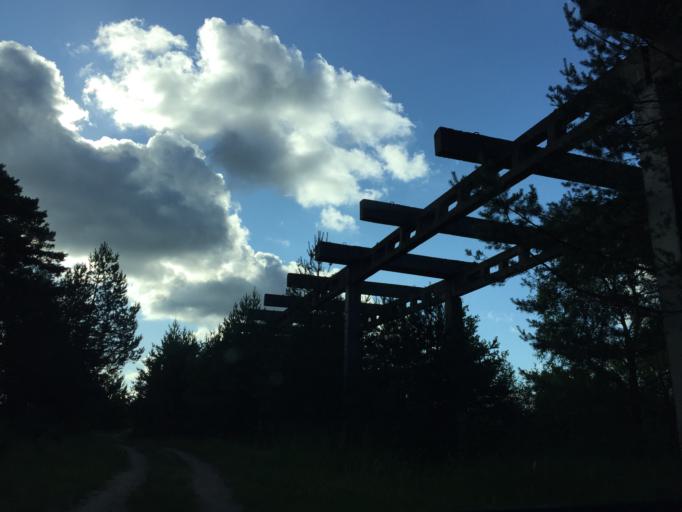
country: LV
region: Ventspils
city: Ventspils
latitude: 57.4099
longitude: 21.6309
